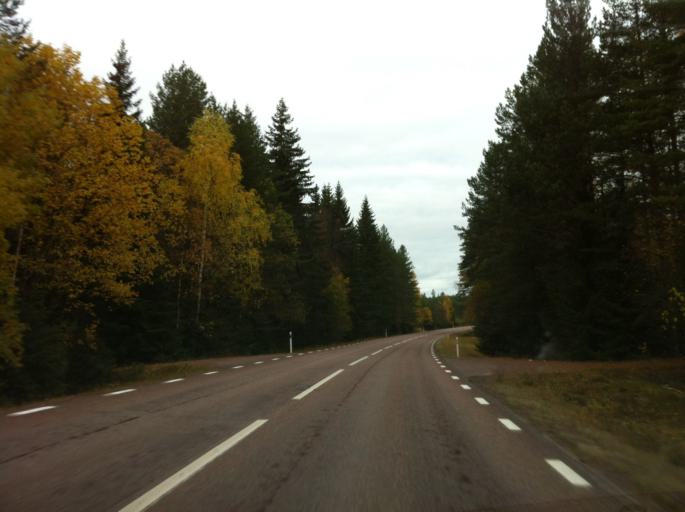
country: SE
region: Dalarna
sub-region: Mora Kommun
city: Mora
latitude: 61.0779
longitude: 14.3516
